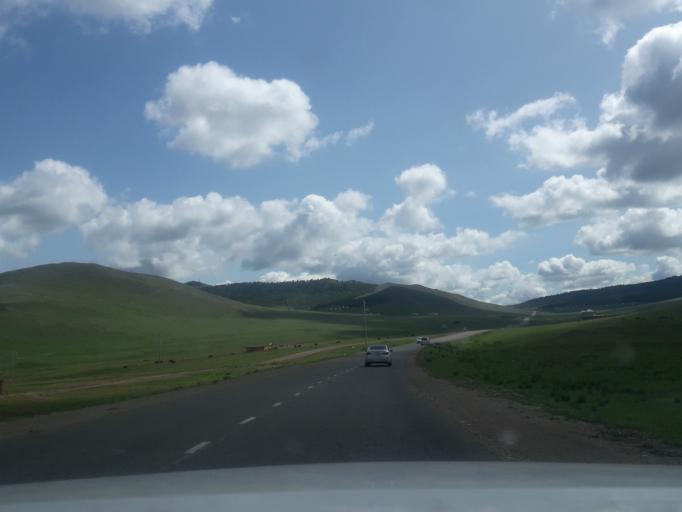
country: MN
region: Central Aimak
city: Ihsueuej
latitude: 48.1728
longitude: 106.4003
